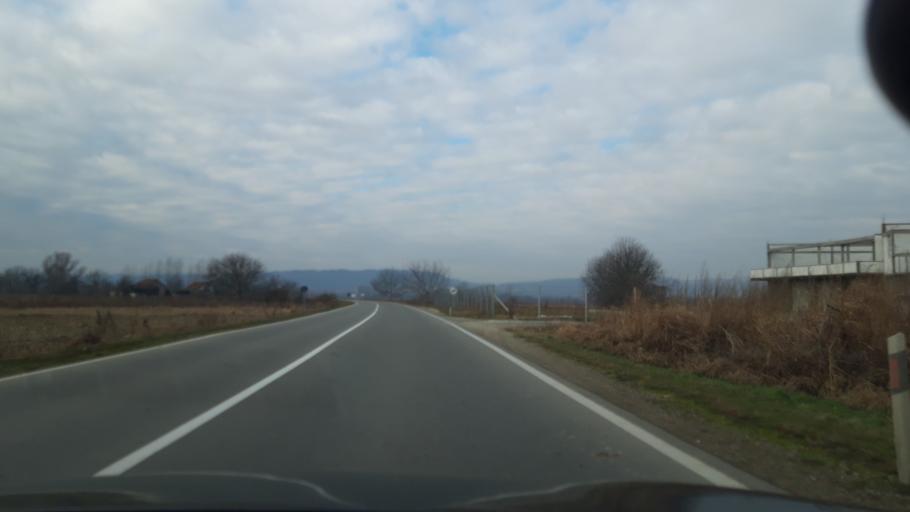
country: RS
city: Lipnicki Sor
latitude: 44.5725
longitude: 19.2205
